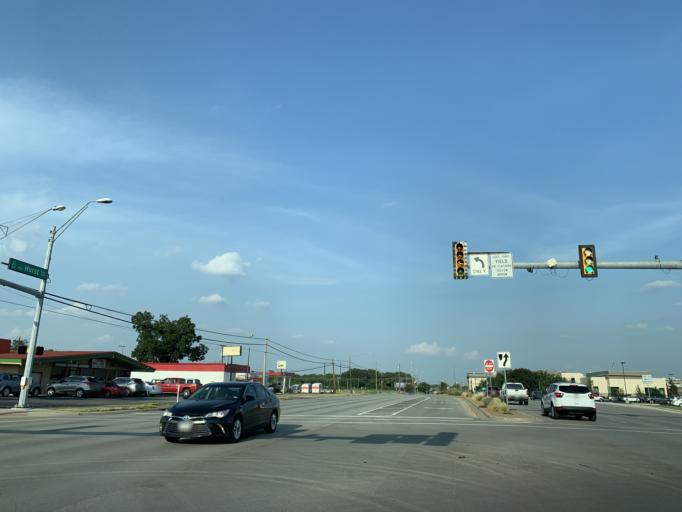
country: US
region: Texas
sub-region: Tarrant County
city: Hurst
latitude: 32.8088
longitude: -97.1627
